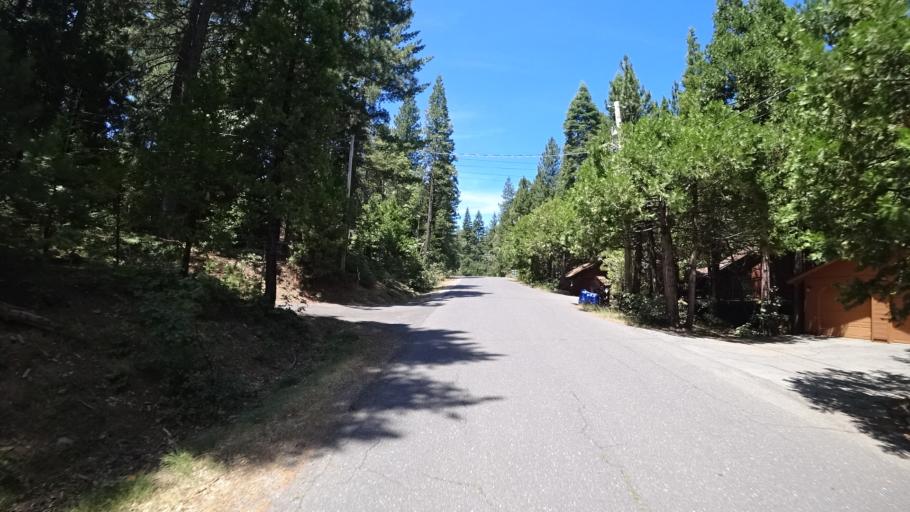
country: US
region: California
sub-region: Calaveras County
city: Arnold
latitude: 38.3044
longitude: -120.2579
